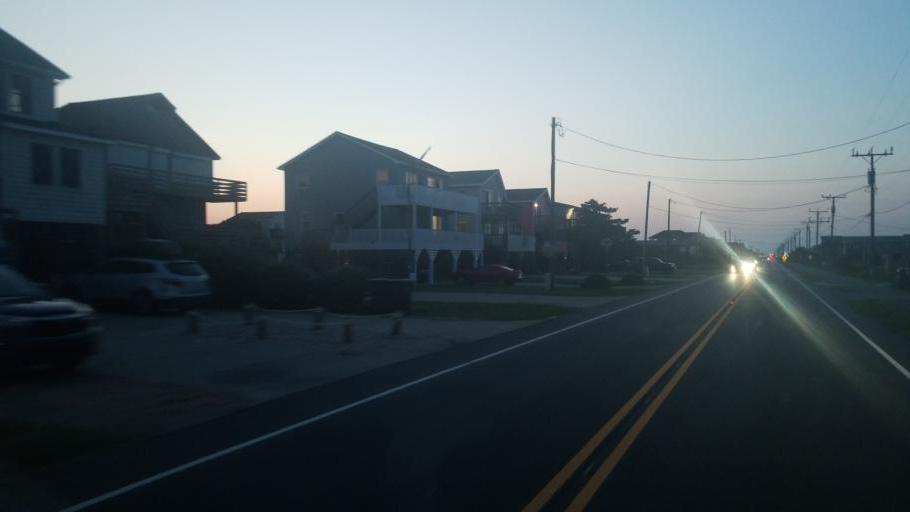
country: US
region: North Carolina
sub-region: Dare County
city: Nags Head
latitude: 35.9908
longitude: -75.6434
